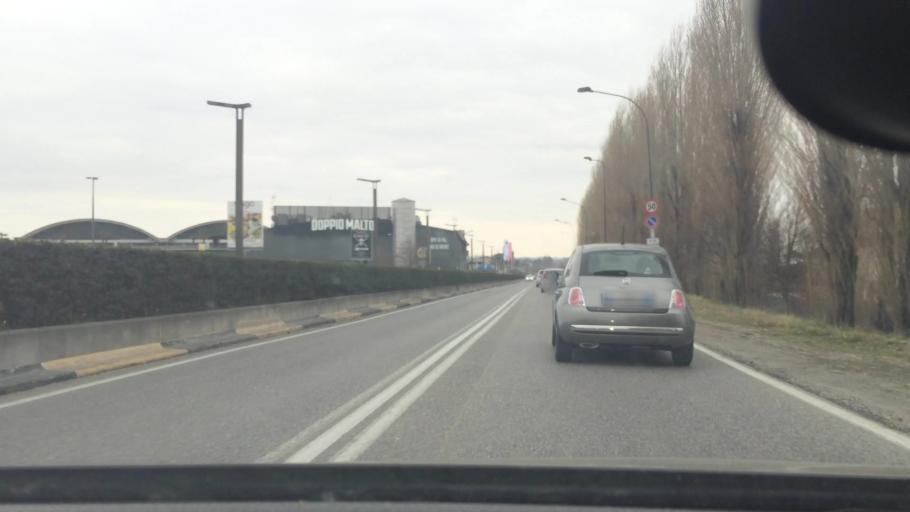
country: IT
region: Lombardy
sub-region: Provincia di Como
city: Erba
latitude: 45.8009
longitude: 9.2377
